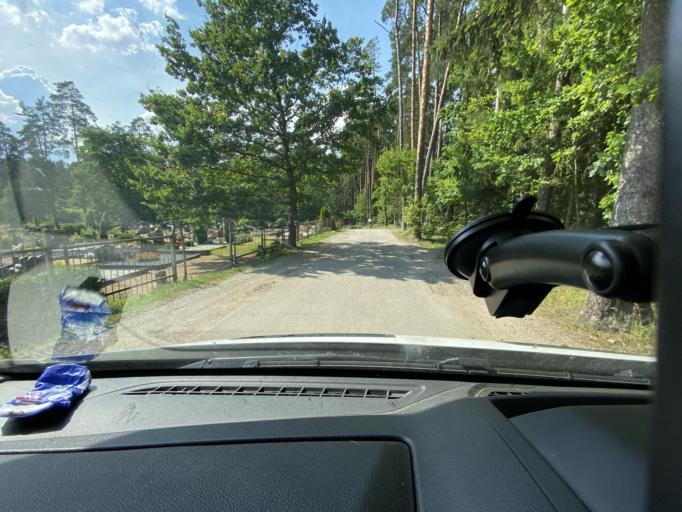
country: LT
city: Ramuciai
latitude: 54.9756
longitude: 24.0405
